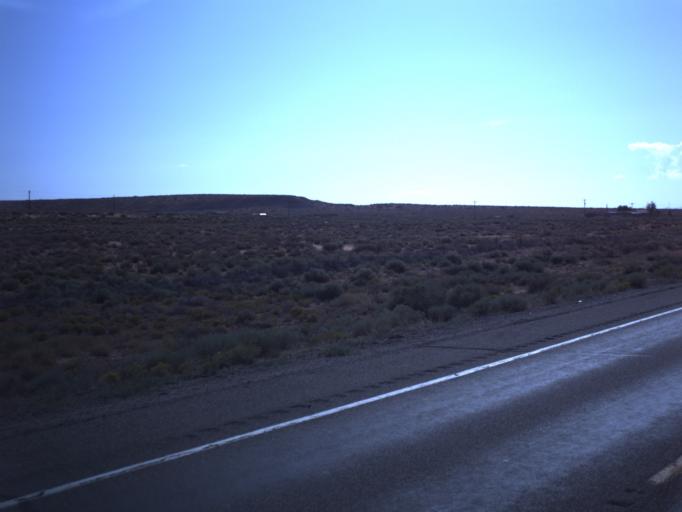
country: US
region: Utah
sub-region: San Juan County
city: Blanding
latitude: 37.1602
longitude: -109.5729
